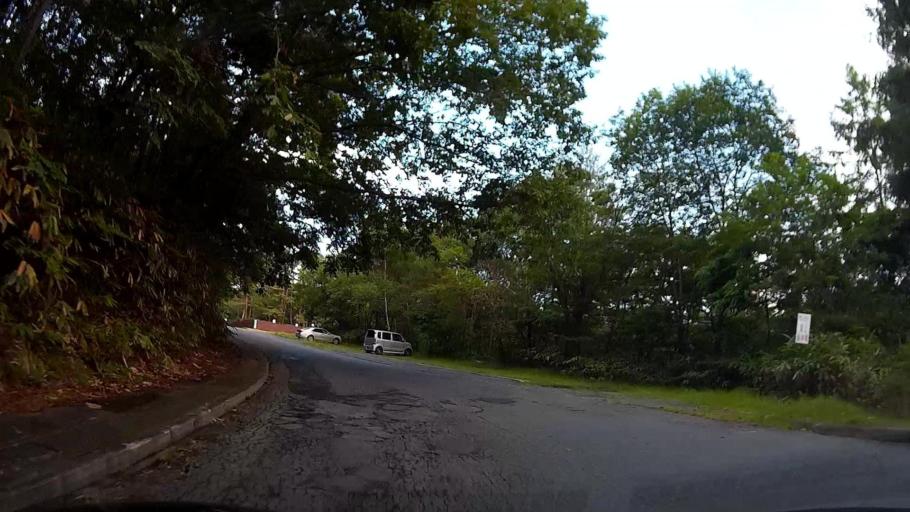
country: JP
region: Gunma
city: Nakanojomachi
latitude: 36.6249
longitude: 138.6083
